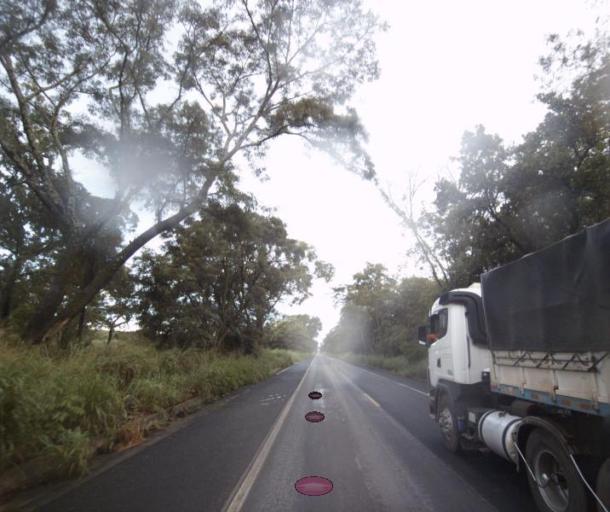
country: BR
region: Goias
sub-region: Porangatu
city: Porangatu
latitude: -13.9118
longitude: -49.0651
